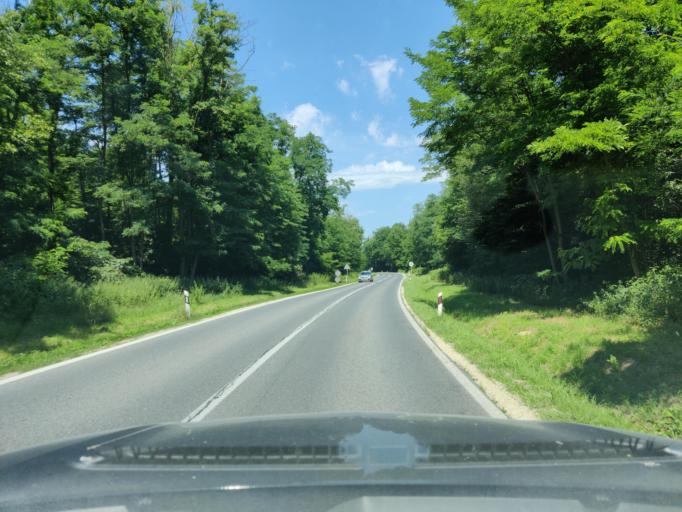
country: HR
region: Medimurska
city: Mackovec
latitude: 46.4539
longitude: 16.4314
